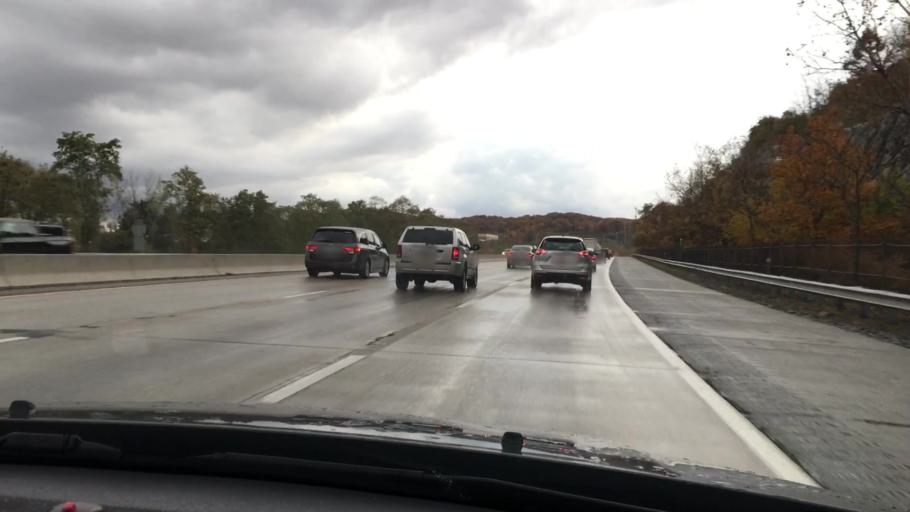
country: US
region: New Jersey
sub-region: Morris County
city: Riverdale
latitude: 41.0017
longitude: -74.3038
